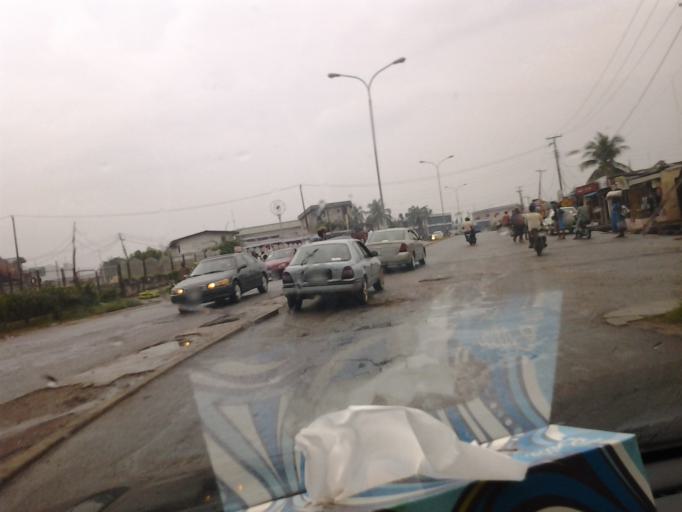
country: NG
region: Oyo
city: Ibadan
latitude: 7.4394
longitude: 3.9073
